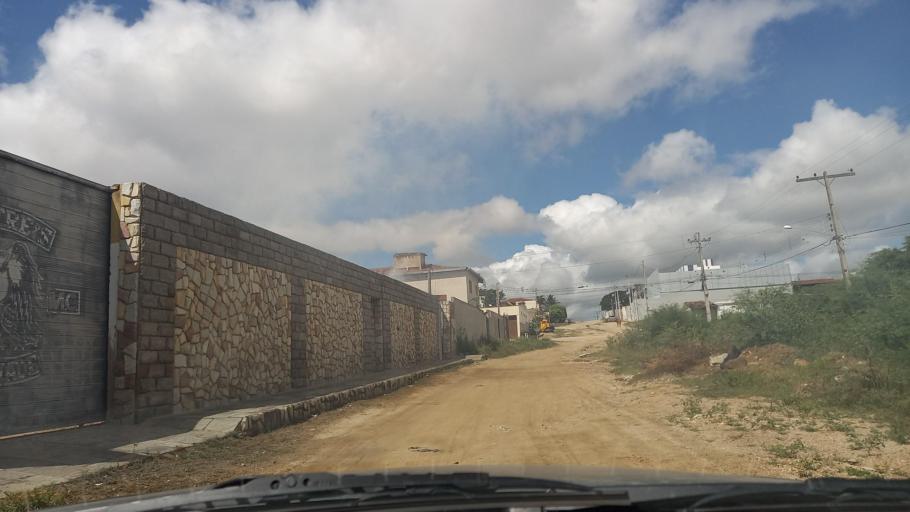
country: BR
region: Pernambuco
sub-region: Caruaru
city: Caruaru
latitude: -8.2543
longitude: -35.9808
